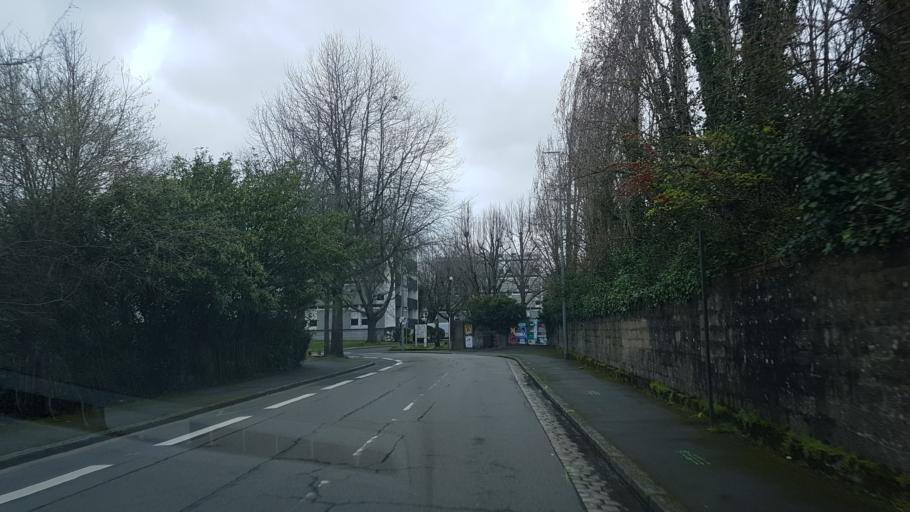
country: FR
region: Pays de la Loire
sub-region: Departement de la Loire-Atlantique
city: Nantes
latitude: 47.2487
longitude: -1.5282
